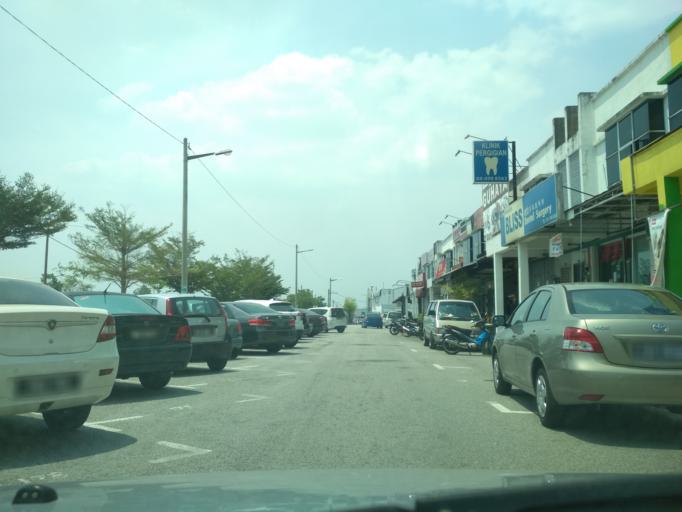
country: MY
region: Kedah
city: Kulim
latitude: 5.3647
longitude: 100.5296
